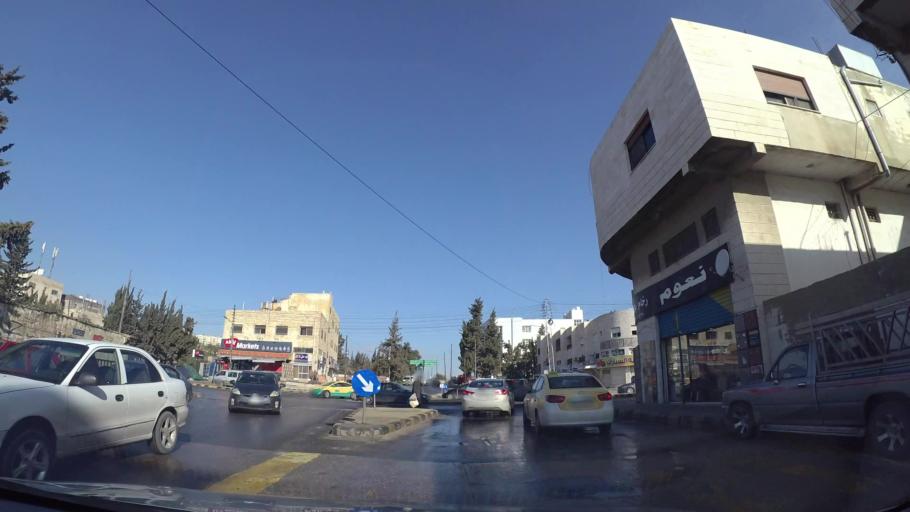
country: JO
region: Amman
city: Al Jubayhah
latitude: 32.0164
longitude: 35.8471
